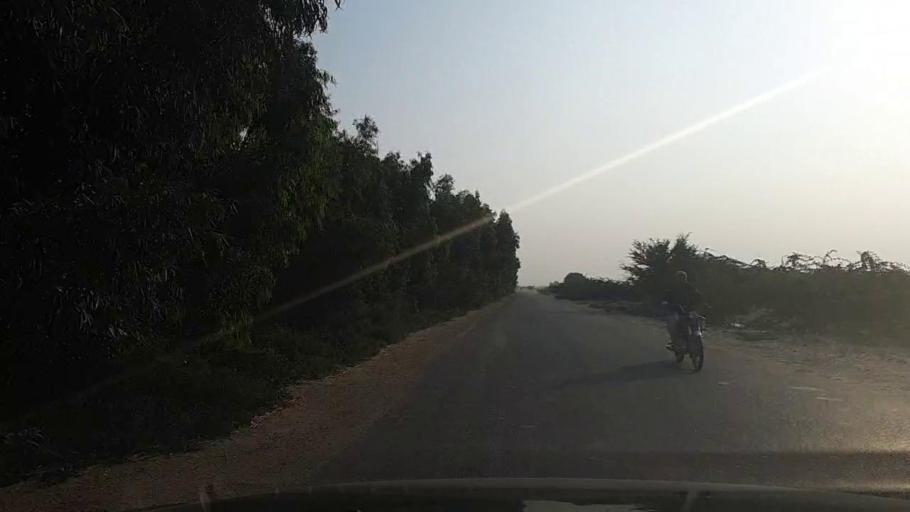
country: PK
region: Sindh
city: Mirpur Sakro
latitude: 24.4990
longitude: 67.8132
